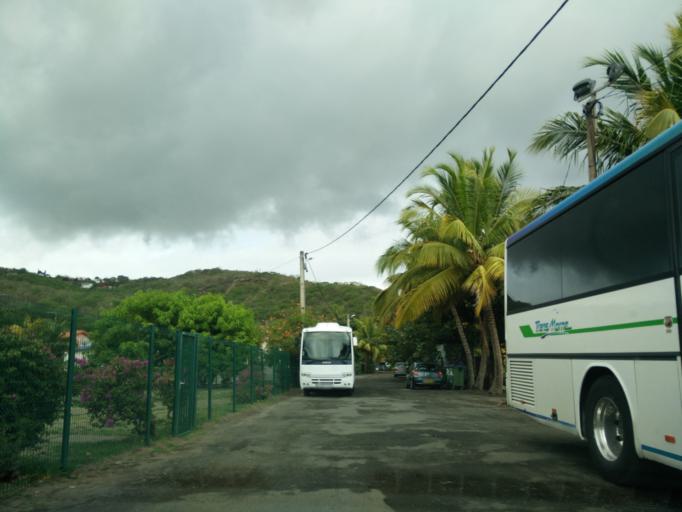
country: MQ
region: Martinique
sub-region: Martinique
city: Saint-Pierre
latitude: 14.6987
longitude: -61.1807
